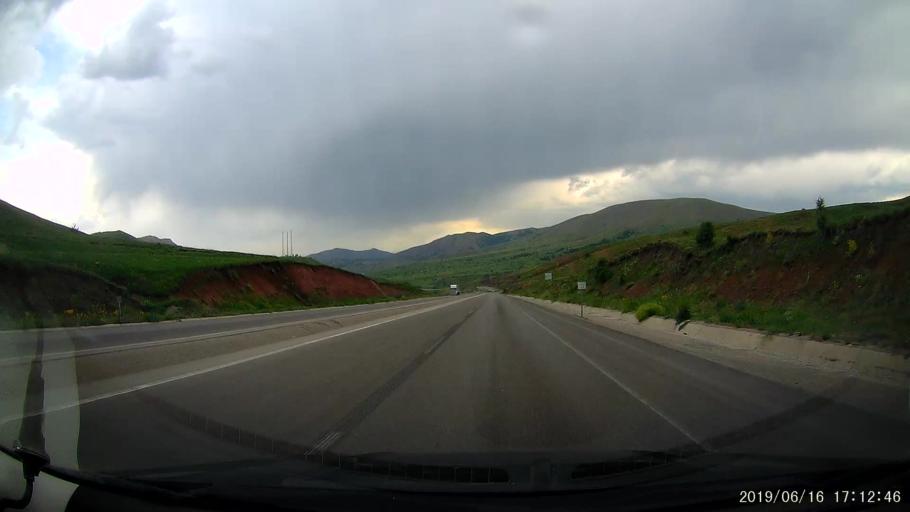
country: TR
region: Erzurum
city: Askale
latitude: 39.8594
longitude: 40.6129
